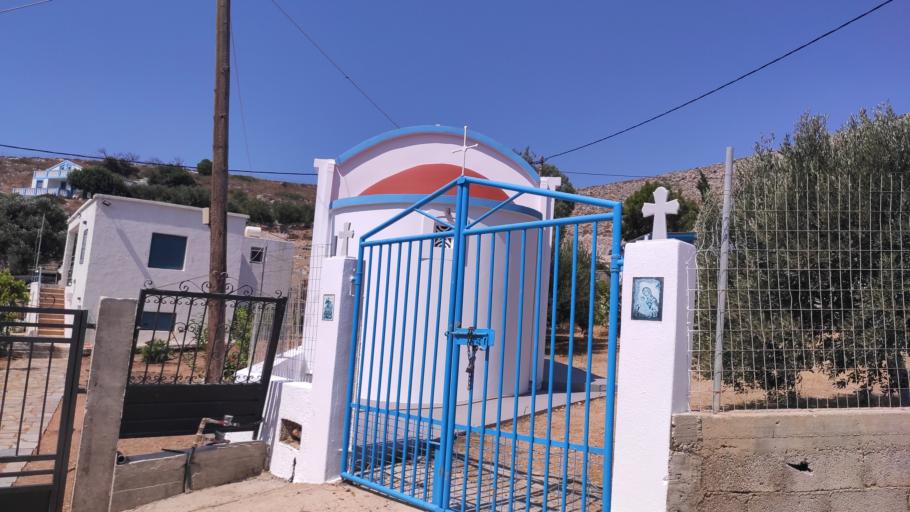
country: GR
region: South Aegean
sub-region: Nomos Dodekanisou
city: Pylion
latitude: 36.9343
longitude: 27.1323
